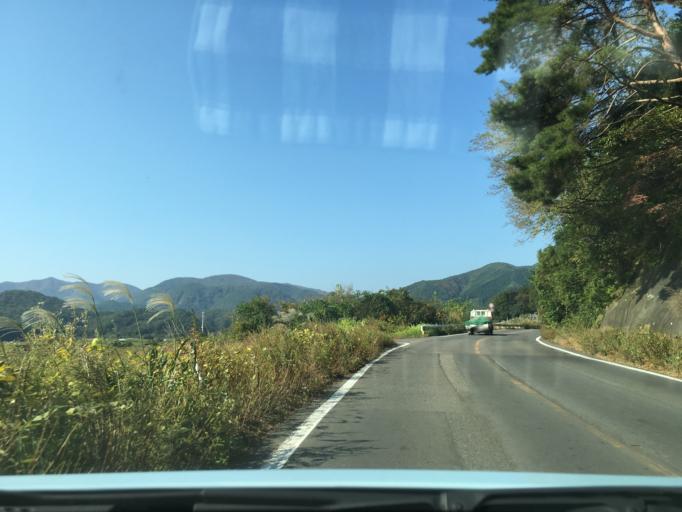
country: JP
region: Fukushima
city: Sukagawa
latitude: 37.2917
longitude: 140.1776
